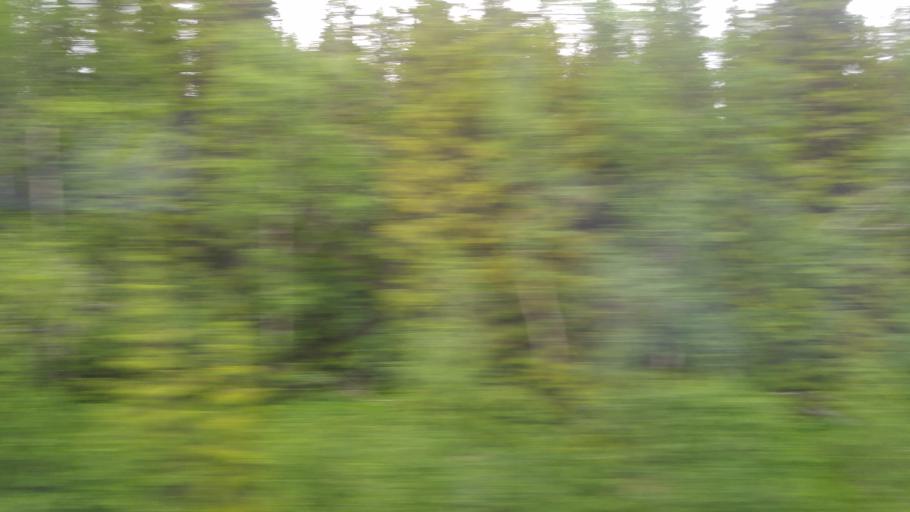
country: NO
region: Nord-Trondelag
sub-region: Meraker
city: Meraker
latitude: 63.2864
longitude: 12.3680
